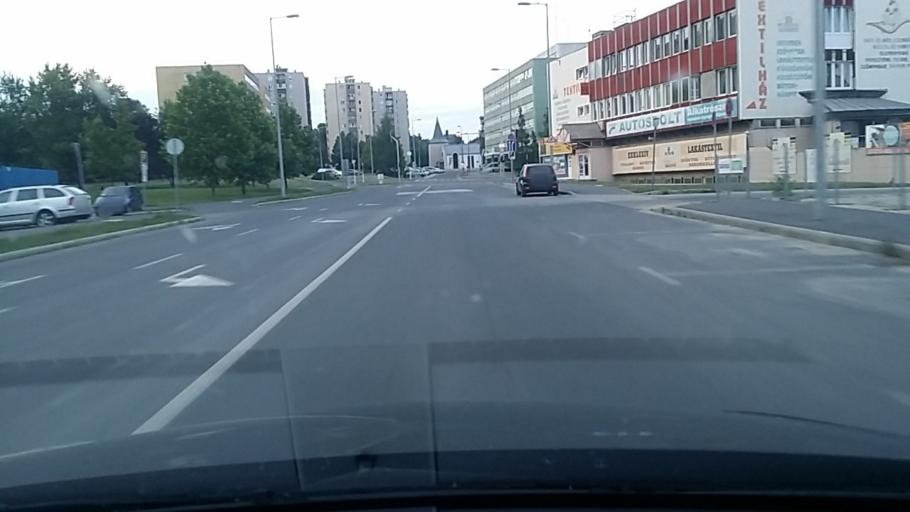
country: HU
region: Borsod-Abauj-Zemplen
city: Miskolc
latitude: 48.1056
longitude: 20.7759
